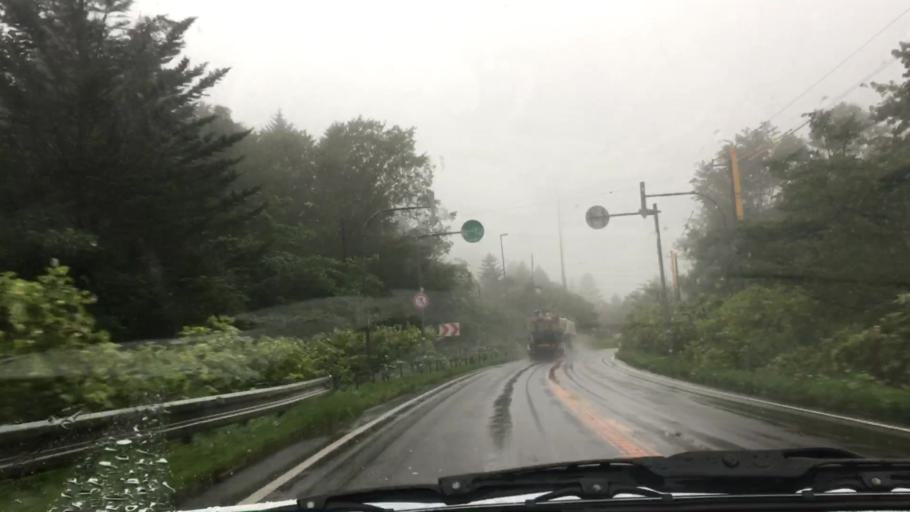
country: JP
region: Hokkaido
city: Niseko Town
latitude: 42.5925
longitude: 140.5156
